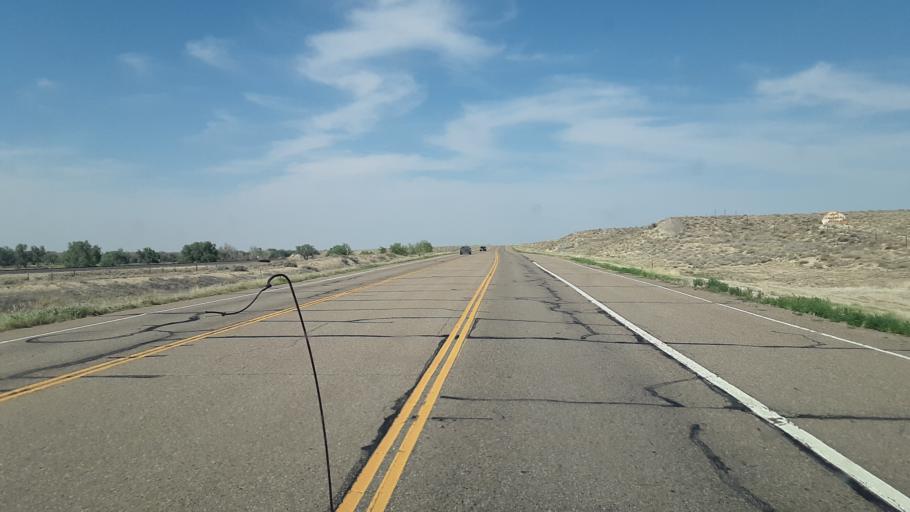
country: US
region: Colorado
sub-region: Otero County
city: La Junta
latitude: 38.0397
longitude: -103.3959
